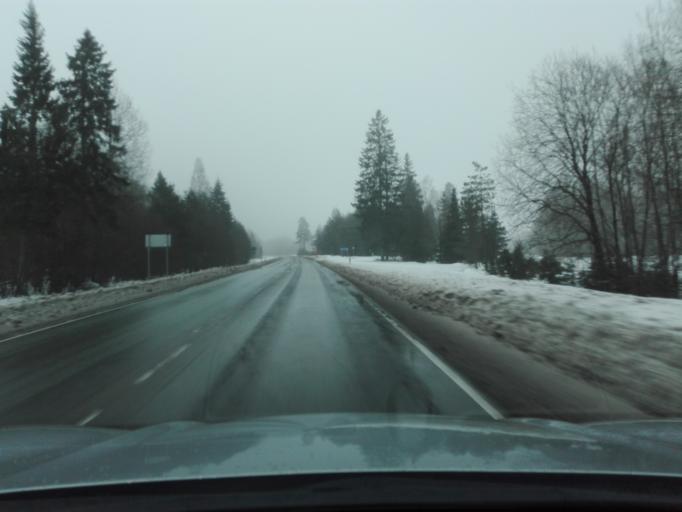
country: EE
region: Raplamaa
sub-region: Kohila vald
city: Kohila
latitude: 59.2452
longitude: 24.7496
